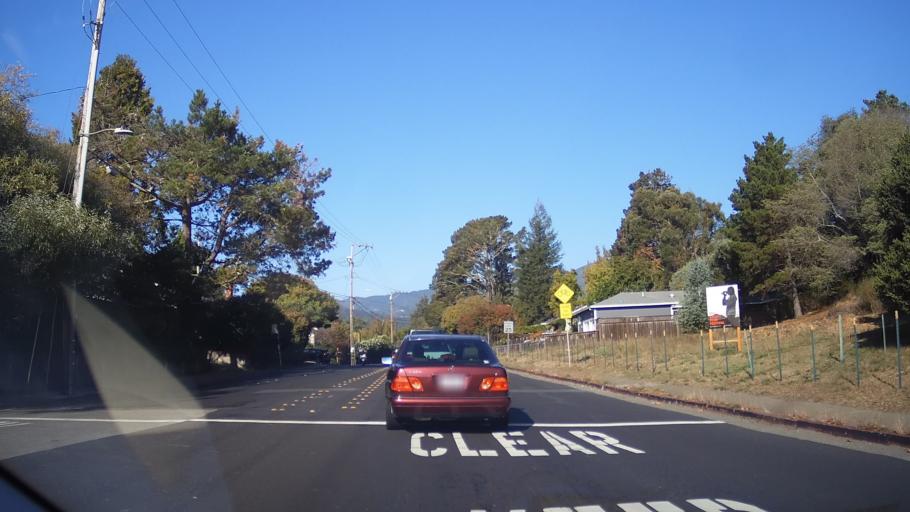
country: US
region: California
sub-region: Marin County
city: Mill Valley
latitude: 37.9006
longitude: -122.5293
